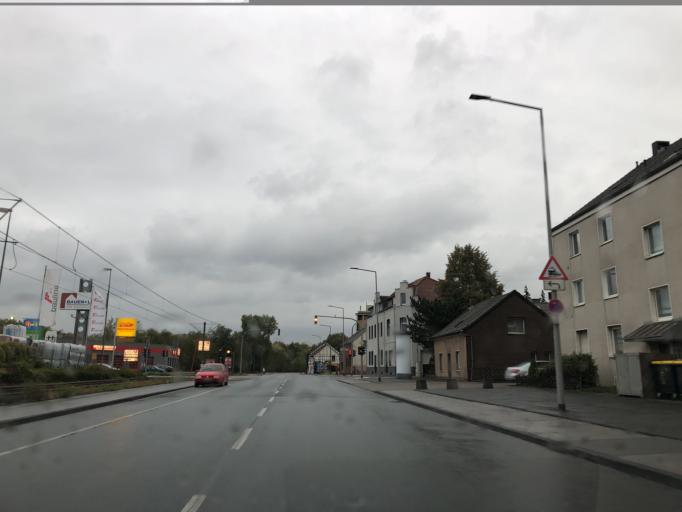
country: DE
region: North Rhine-Westphalia
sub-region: Regierungsbezirk Dusseldorf
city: Hochfeld
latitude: 51.3793
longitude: 6.7368
